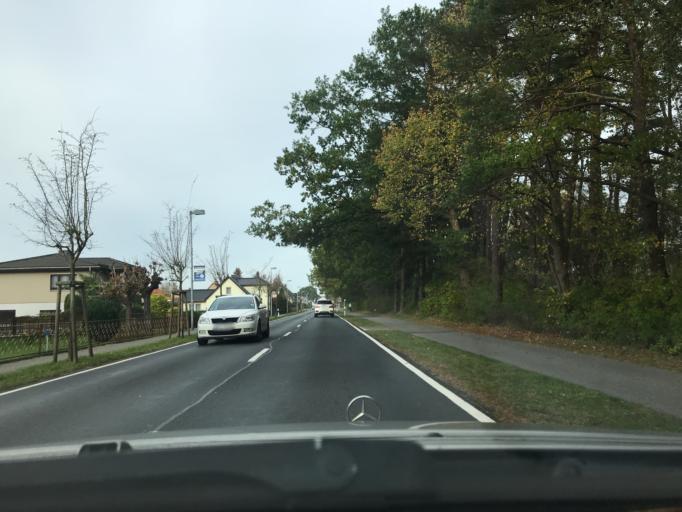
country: DE
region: Mecklenburg-Vorpommern
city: Karlshagen
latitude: 54.1115
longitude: 13.8370
